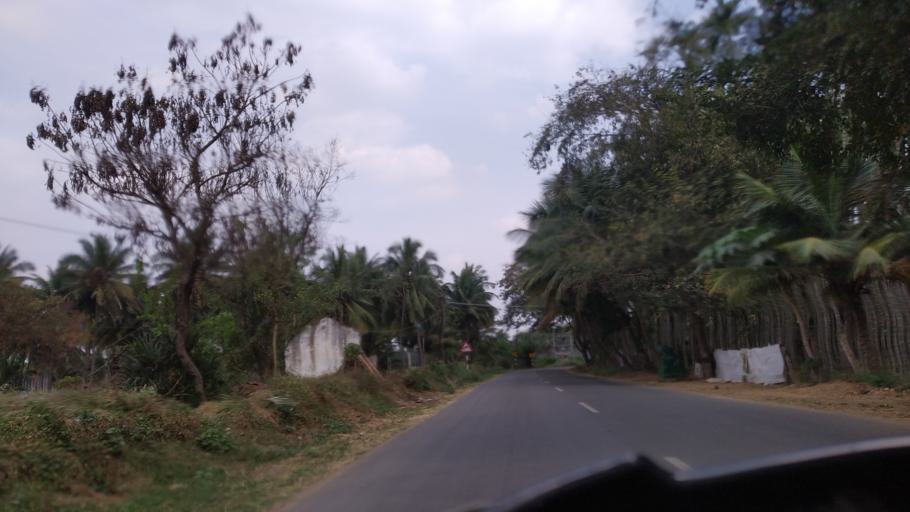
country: IN
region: Tamil Nadu
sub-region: Coimbatore
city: Perur
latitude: 10.9620
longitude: 76.7484
